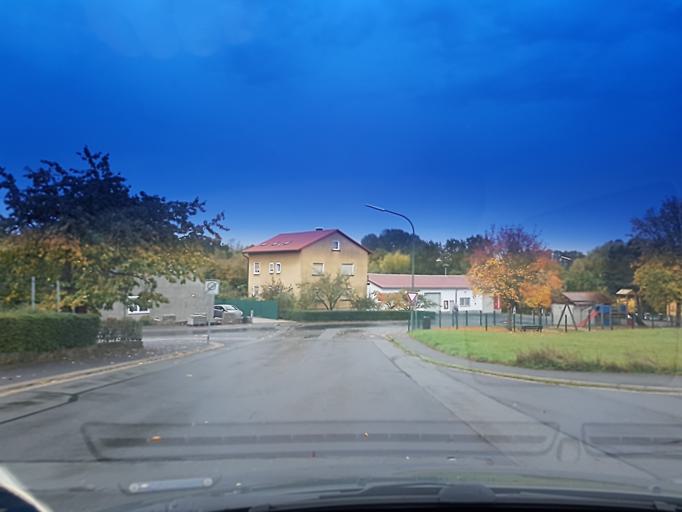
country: DE
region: Bavaria
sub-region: Upper Franconia
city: Schlusselfeld
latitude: 49.7539
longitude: 10.6323
